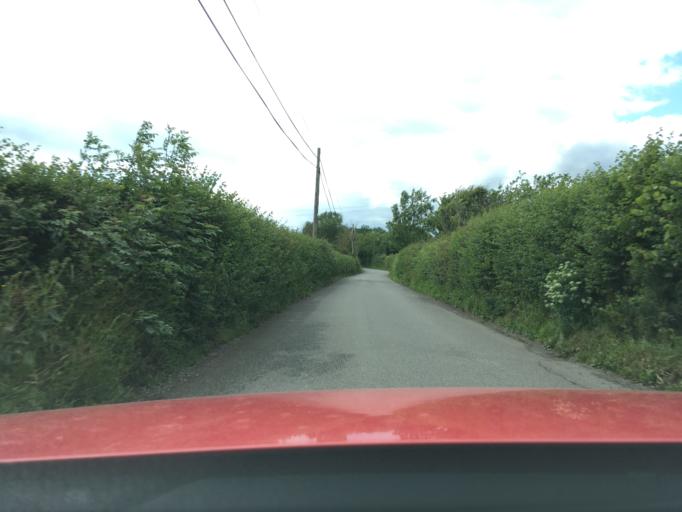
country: GB
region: England
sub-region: Gloucestershire
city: Cinderford
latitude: 51.7938
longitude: -2.4095
